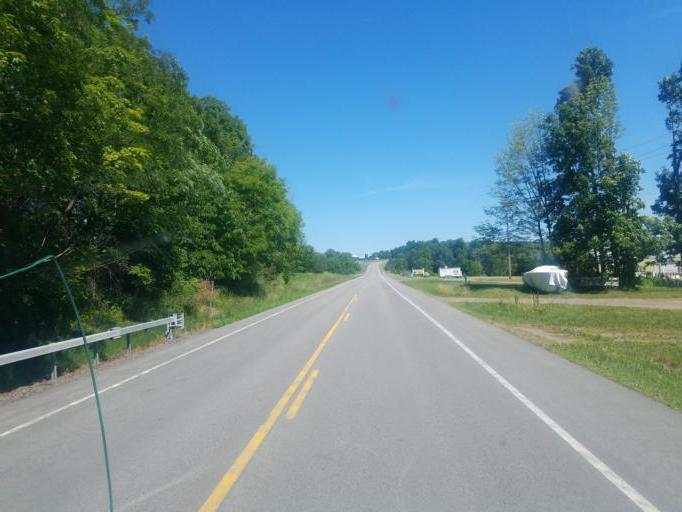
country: US
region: New York
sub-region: Ontario County
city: Canandaigua
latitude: 42.7199
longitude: -77.2770
